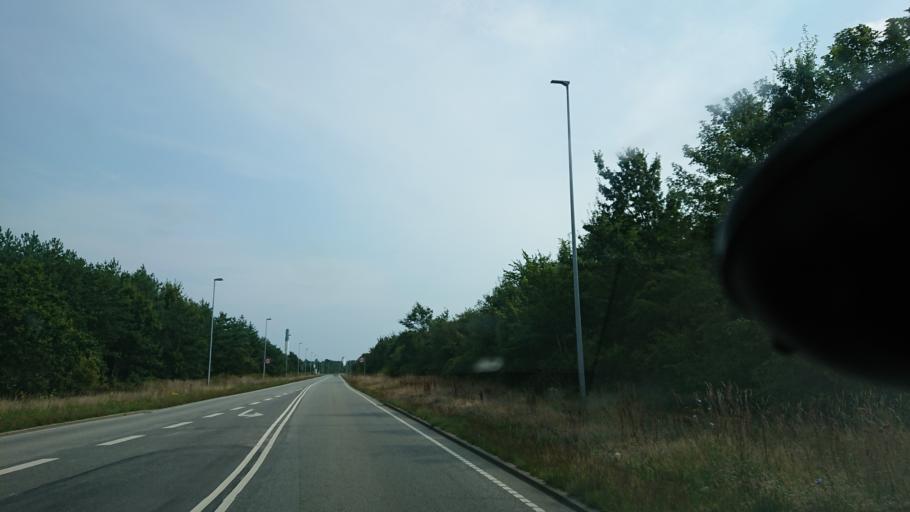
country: DK
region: North Denmark
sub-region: Frederikshavn Kommune
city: Frederikshavn
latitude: 57.4563
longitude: 10.5092
